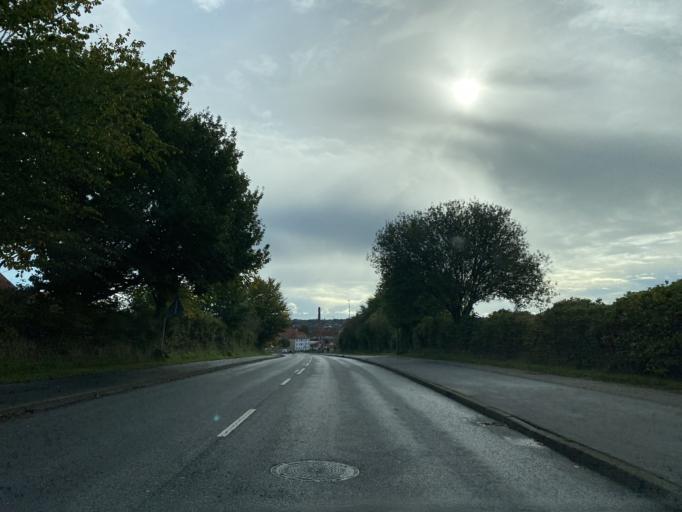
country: DK
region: South Denmark
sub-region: Haderslev Kommune
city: Haderslev
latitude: 55.2566
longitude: 9.4783
